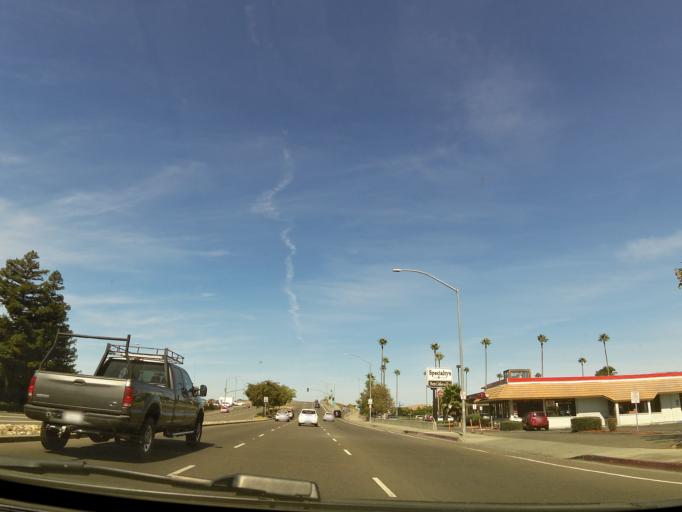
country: US
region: California
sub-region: Alameda County
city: Dublin
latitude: 37.6991
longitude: -121.9046
